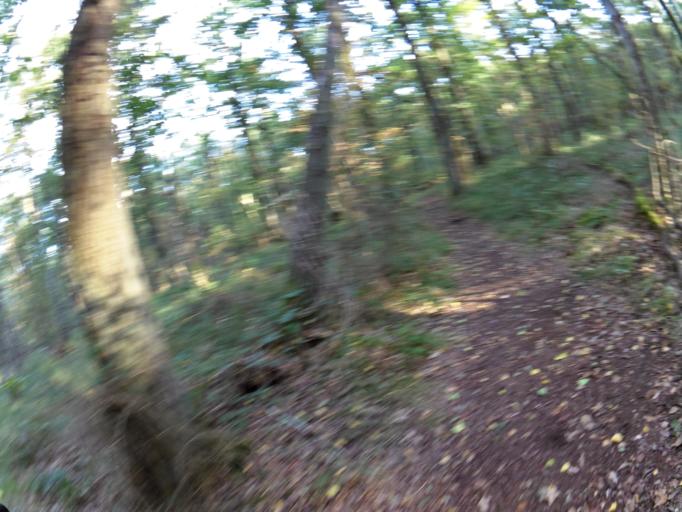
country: DE
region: North Rhine-Westphalia
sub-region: Regierungsbezirk Koln
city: Gangelt
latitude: 50.9684
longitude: 6.0129
